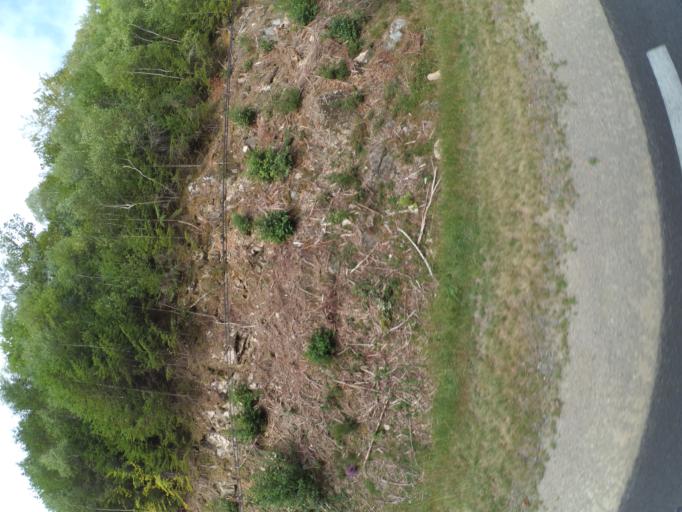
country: FR
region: Limousin
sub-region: Departement de la Correze
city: Meymac
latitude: 45.5579
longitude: 2.1472
